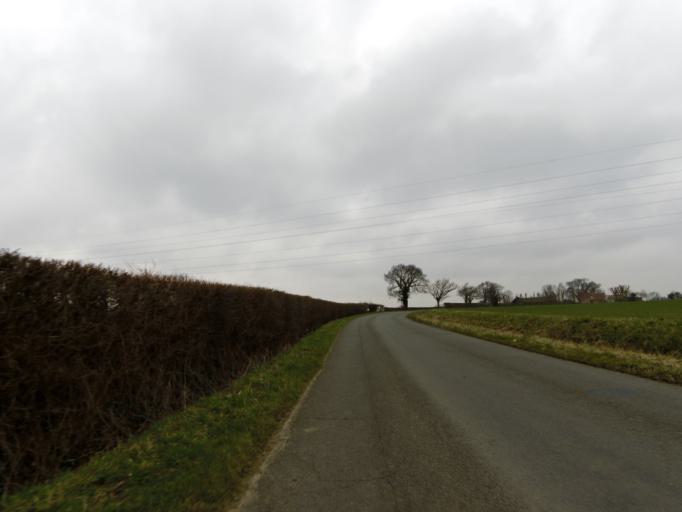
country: GB
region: England
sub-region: Suffolk
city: Framlingham
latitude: 52.2039
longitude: 1.3297
